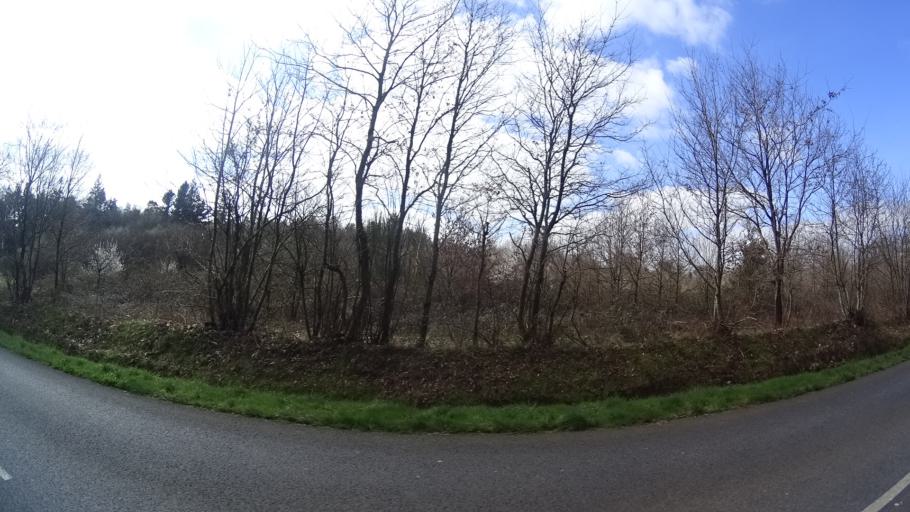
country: FR
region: Brittany
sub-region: Departement du Morbihan
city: Caro
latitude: 47.8507
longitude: -2.3335
